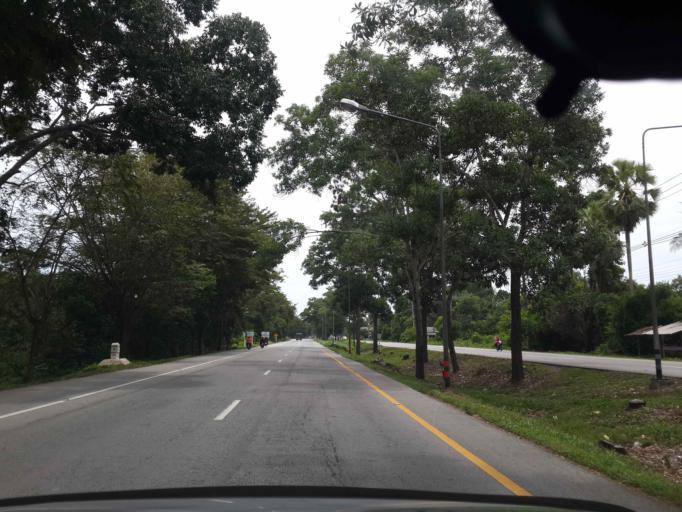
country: TH
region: Narathiwat
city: Yi-ngo
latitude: 6.4050
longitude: 101.7444
